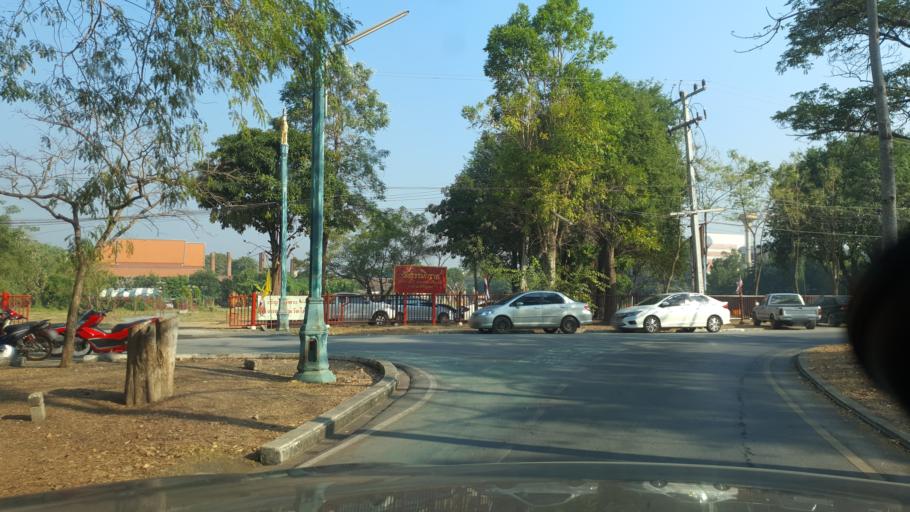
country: TH
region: Phra Nakhon Si Ayutthaya
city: Phra Nakhon Si Ayutthaya
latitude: 14.3571
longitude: 100.5618
